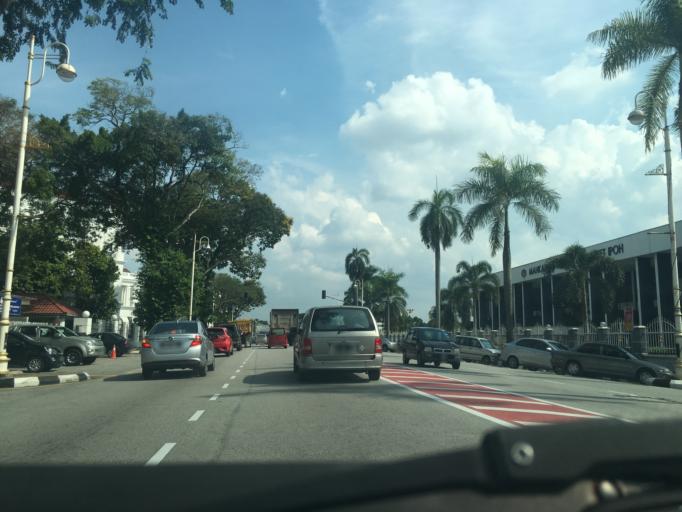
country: MY
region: Perak
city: Ipoh
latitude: 4.5994
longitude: 101.0751
